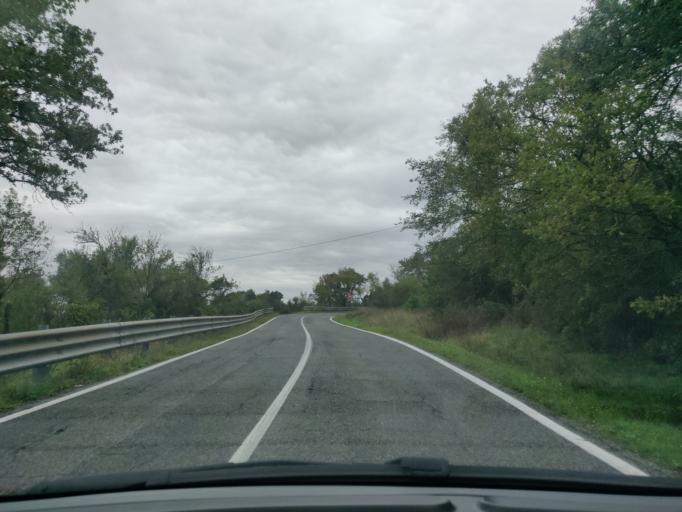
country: IT
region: Latium
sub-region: Citta metropolitana di Roma Capitale
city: Allumiere
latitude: 42.1468
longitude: 11.8962
